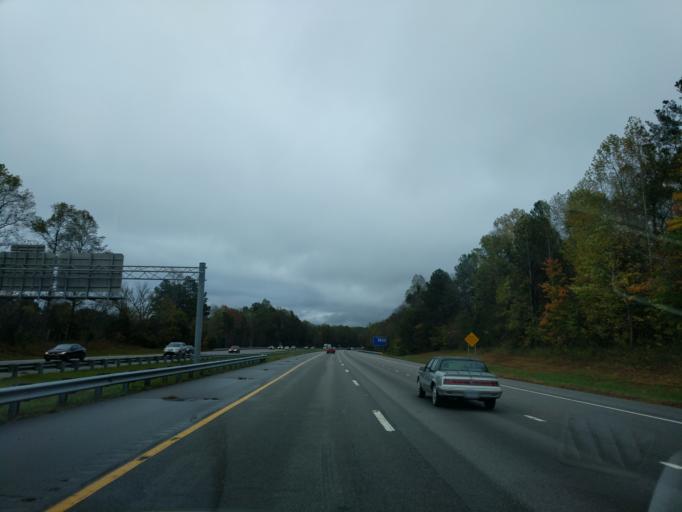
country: US
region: North Carolina
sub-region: Orange County
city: Hillsborough
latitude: 36.0592
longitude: -79.1171
